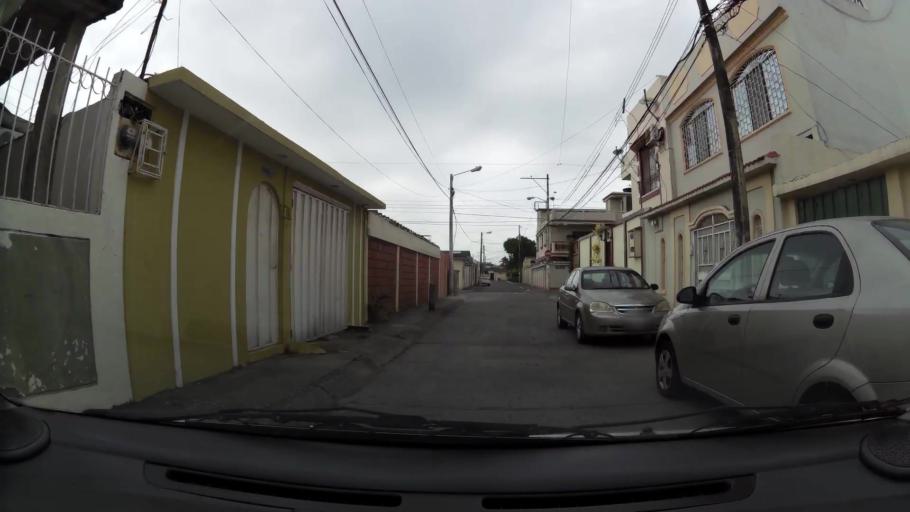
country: EC
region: Guayas
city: Eloy Alfaro
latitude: -2.1203
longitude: -79.8877
